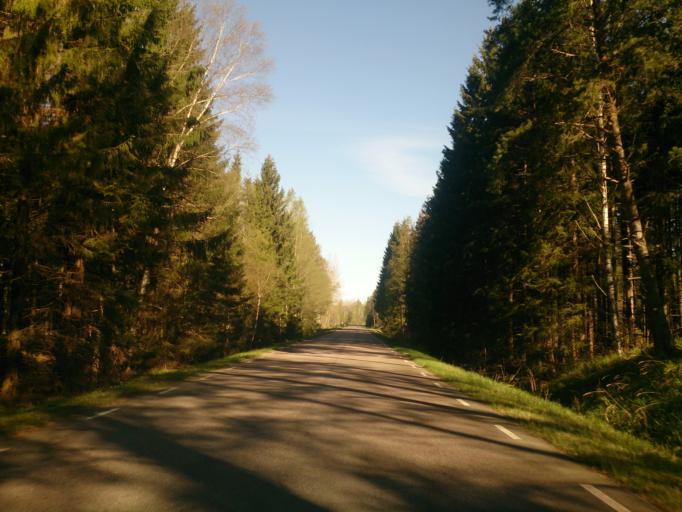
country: SE
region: OEstergoetland
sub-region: Linkopings Kommun
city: Ljungsbro
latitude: 58.6019
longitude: 15.4879
